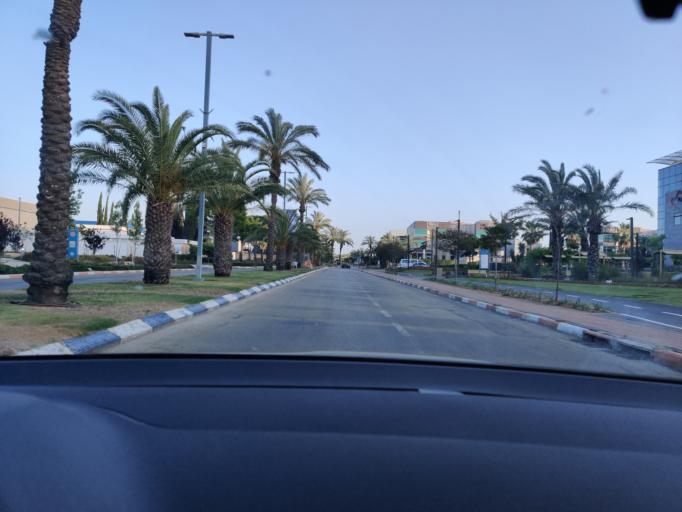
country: IL
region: Haifa
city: Qesarya
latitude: 32.4854
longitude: 34.9480
